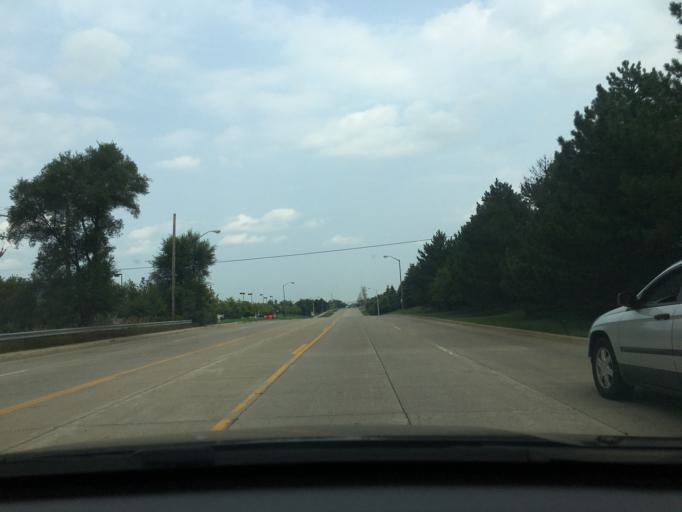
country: US
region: Michigan
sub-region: Oakland County
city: Bloomfield Hills
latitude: 42.6197
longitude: -83.2566
